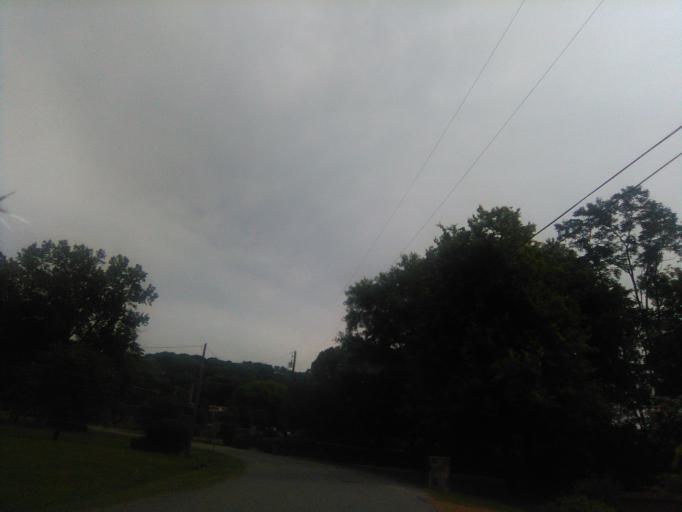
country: US
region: Tennessee
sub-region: Davidson County
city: Belle Meade
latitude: 36.0902
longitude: -86.8942
